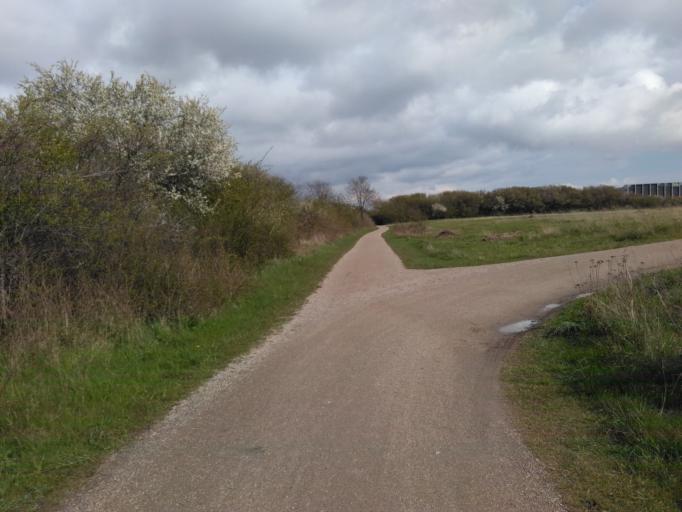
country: DK
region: Capital Region
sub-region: Tarnby Kommune
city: Tarnby
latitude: 55.6443
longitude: 12.5752
